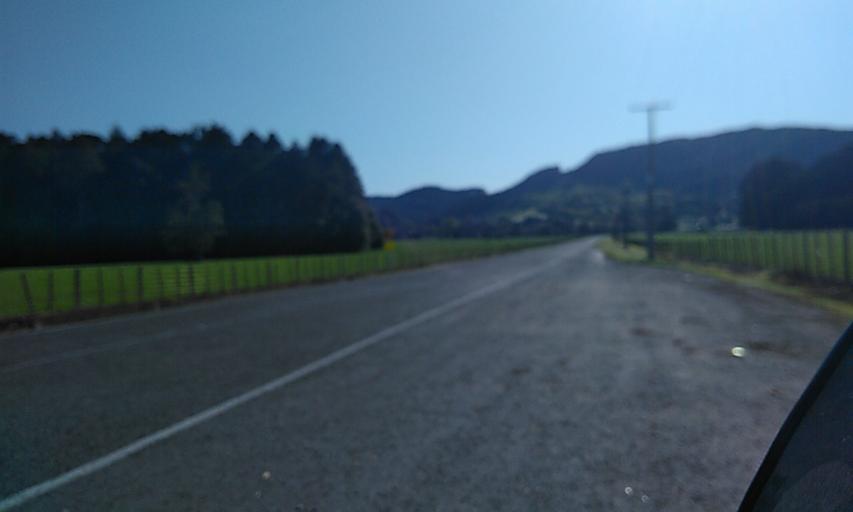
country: NZ
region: Gisborne
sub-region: Gisborne District
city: Gisborne
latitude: -38.5997
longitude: 177.9604
